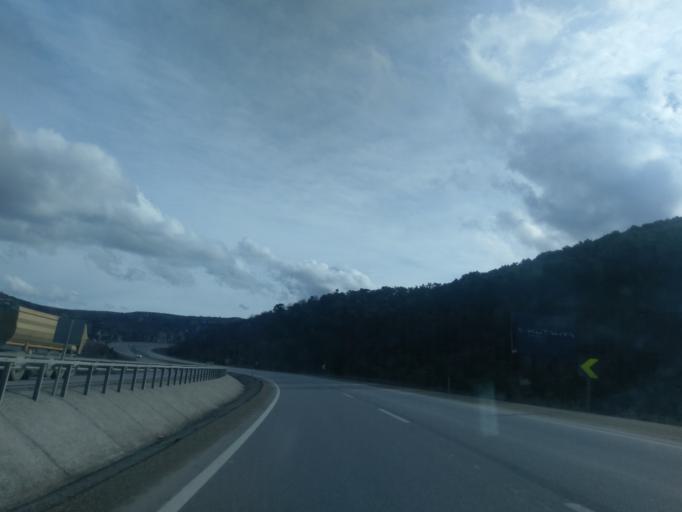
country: TR
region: Kuetahya
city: Sabuncu
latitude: 39.5652
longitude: 30.0721
